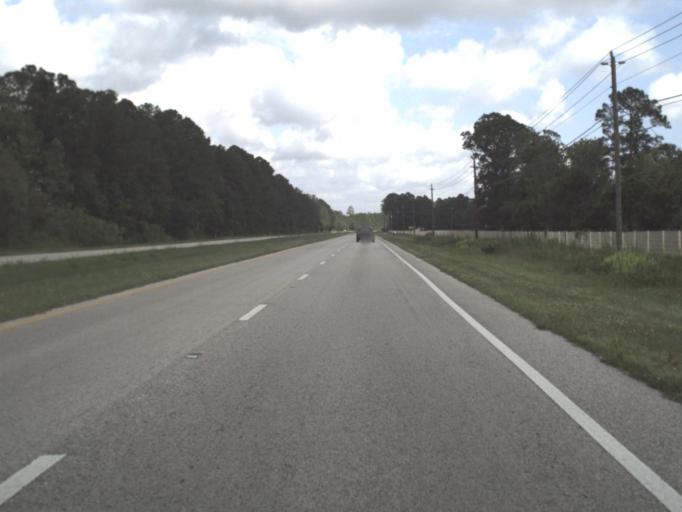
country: US
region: Florida
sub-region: Saint Johns County
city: Butler Beach
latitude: 29.7187
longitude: -81.3037
